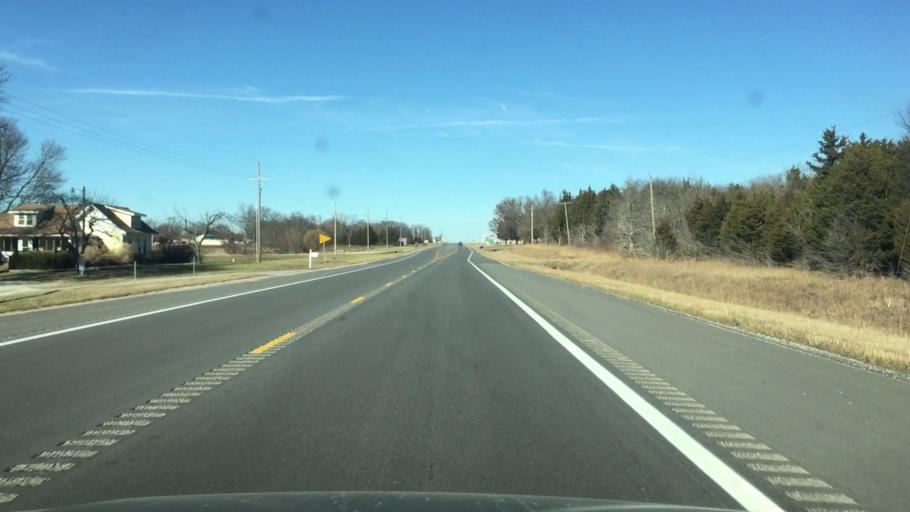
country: US
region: Kansas
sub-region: Franklin County
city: Ottawa
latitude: 38.4826
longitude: -95.2674
